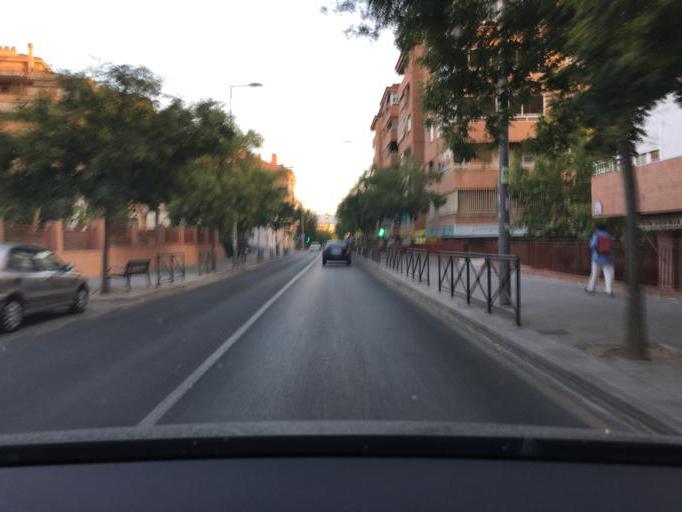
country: ES
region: Andalusia
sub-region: Provincia de Granada
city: Granada
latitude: 37.1910
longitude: -3.6039
